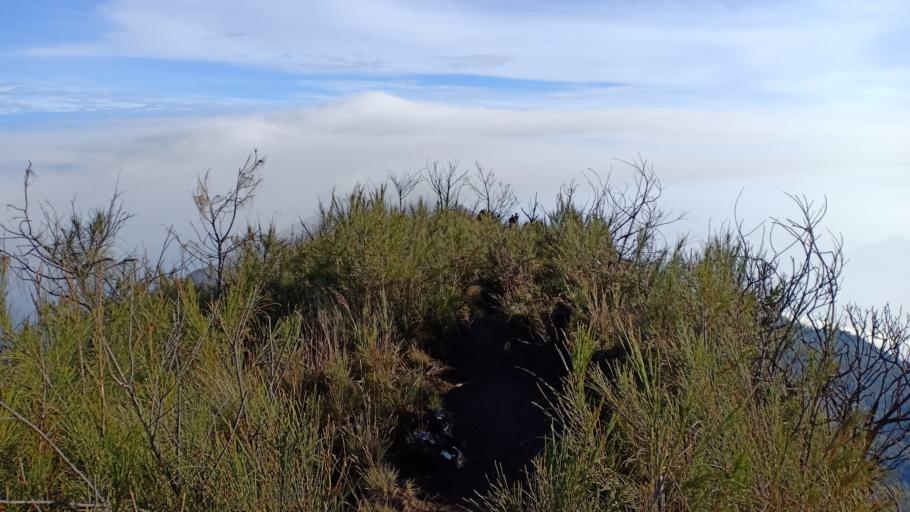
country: ID
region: East Java
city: Prigen
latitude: -7.7638
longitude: 112.5890
